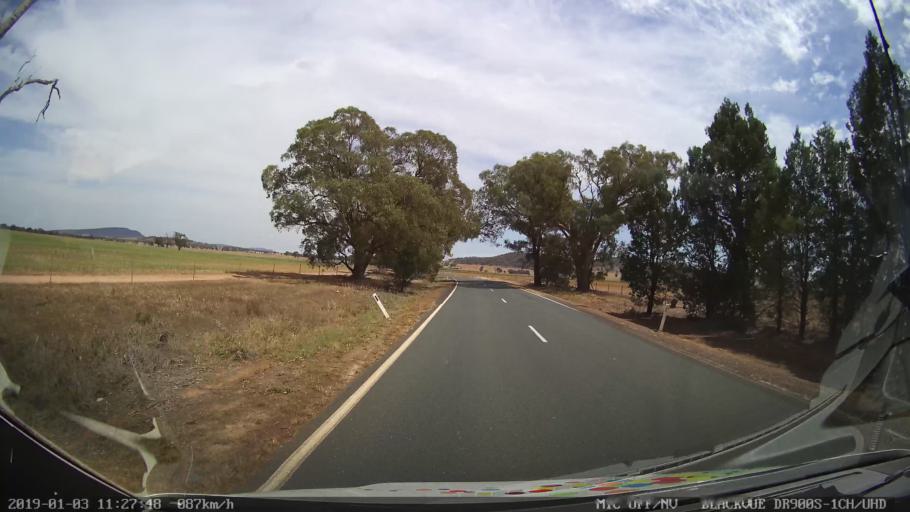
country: AU
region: New South Wales
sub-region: Weddin
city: Grenfell
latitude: -34.0085
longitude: 148.2161
